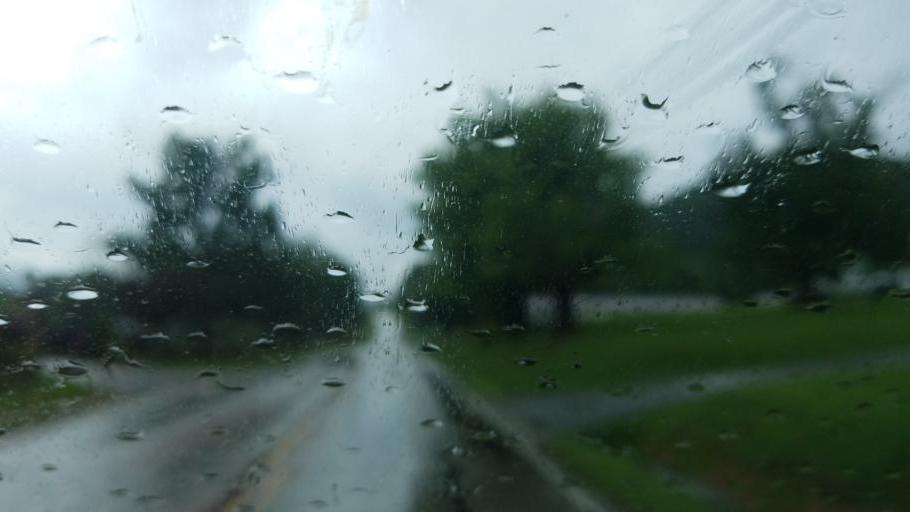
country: US
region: Kentucky
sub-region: Rowan County
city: Morehead
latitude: 38.1599
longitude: -83.4517
